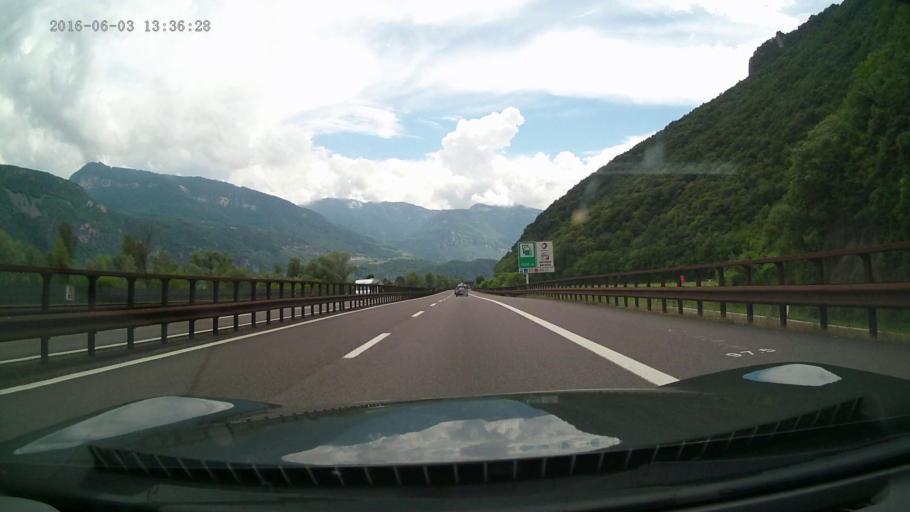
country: IT
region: Trentino-Alto Adige
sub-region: Bolzano
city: Ora
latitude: 46.3714
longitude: 11.2904
